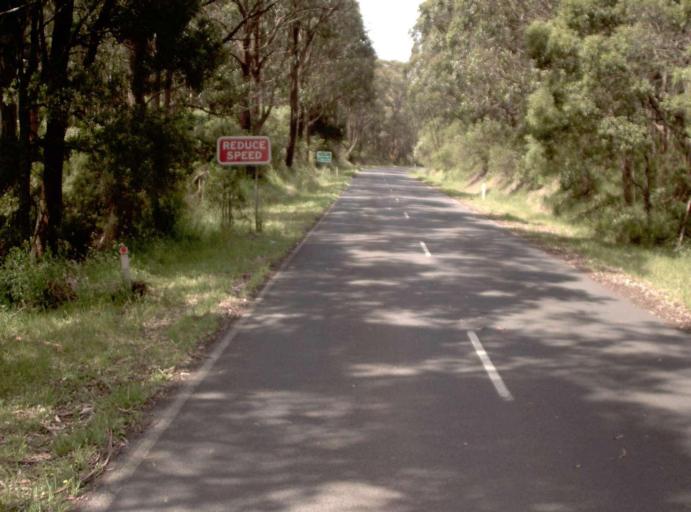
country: AU
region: Victoria
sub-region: Latrobe
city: Traralgon
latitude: -38.3517
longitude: 146.7119
